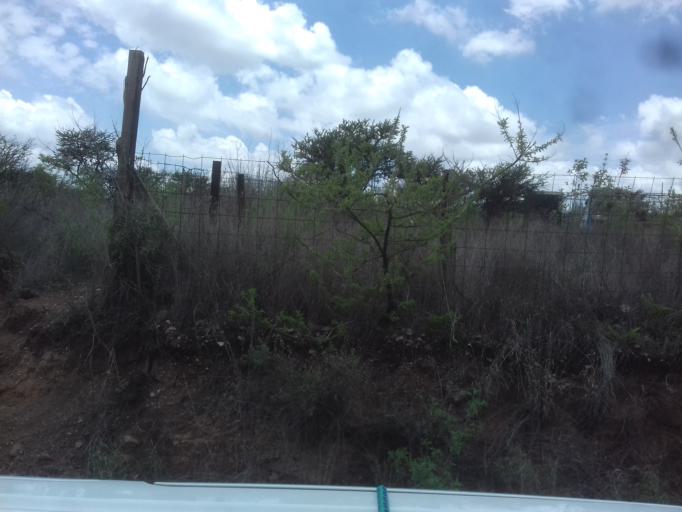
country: MX
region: Aguascalientes
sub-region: Aguascalientes
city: San Sebastian [Fraccionamiento]
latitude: 21.7863
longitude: -102.2505
